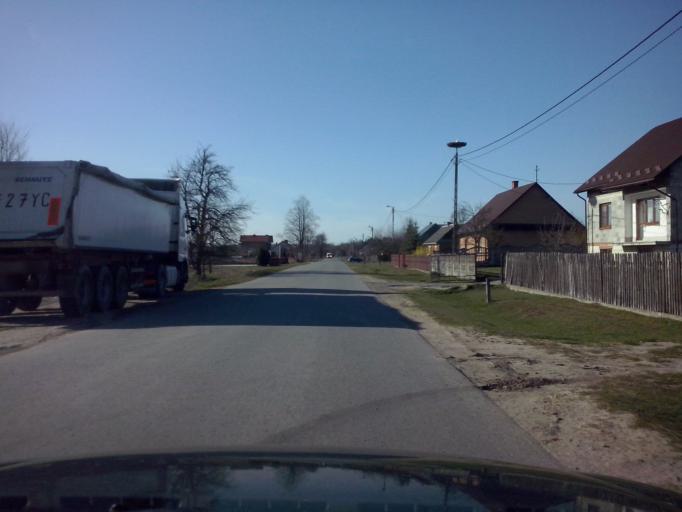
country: PL
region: Subcarpathian Voivodeship
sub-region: Powiat lezajski
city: Stare Miasto
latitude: 50.3539
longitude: 22.4213
